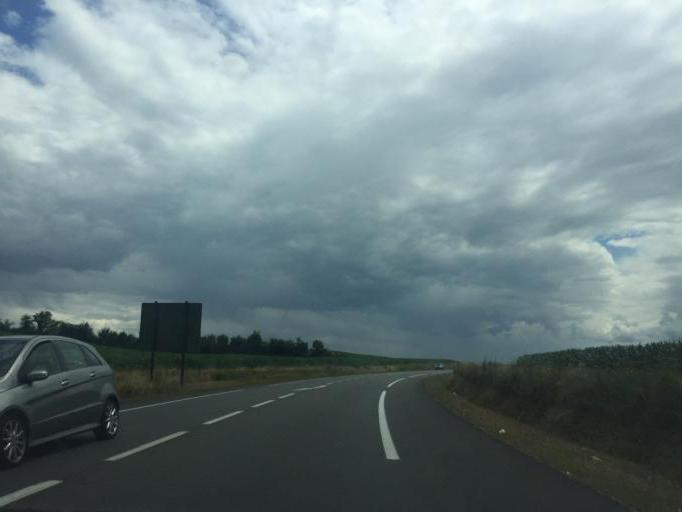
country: FR
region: Rhone-Alpes
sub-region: Departement de l'Isere
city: Janneyrias
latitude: 45.7667
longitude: 5.1197
